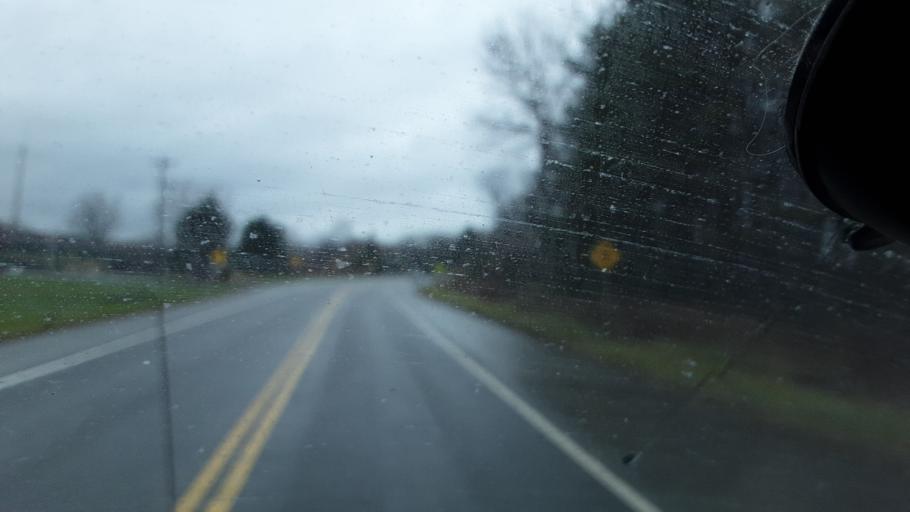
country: US
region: New York
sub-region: Cattaraugus County
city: Yorkshire
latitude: 42.5831
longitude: -78.4888
